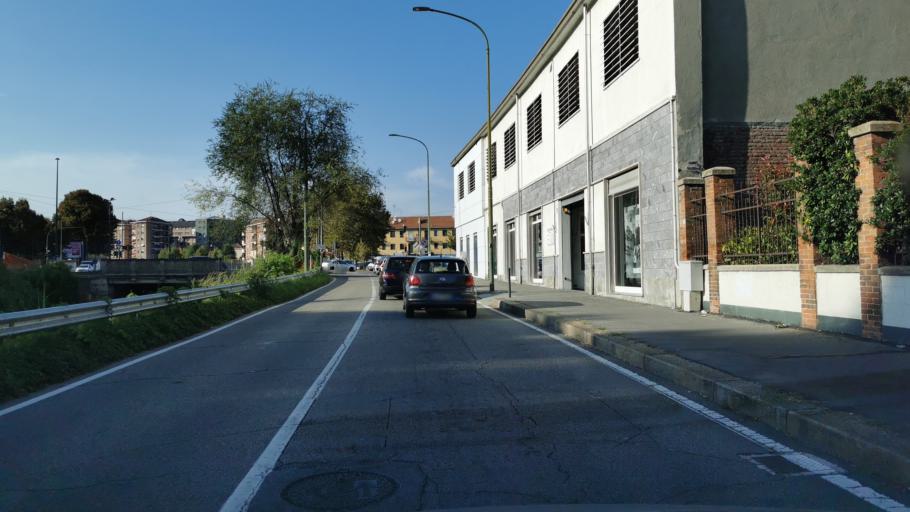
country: IT
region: Piedmont
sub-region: Provincia di Torino
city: Turin
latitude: 45.0899
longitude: 7.7127
